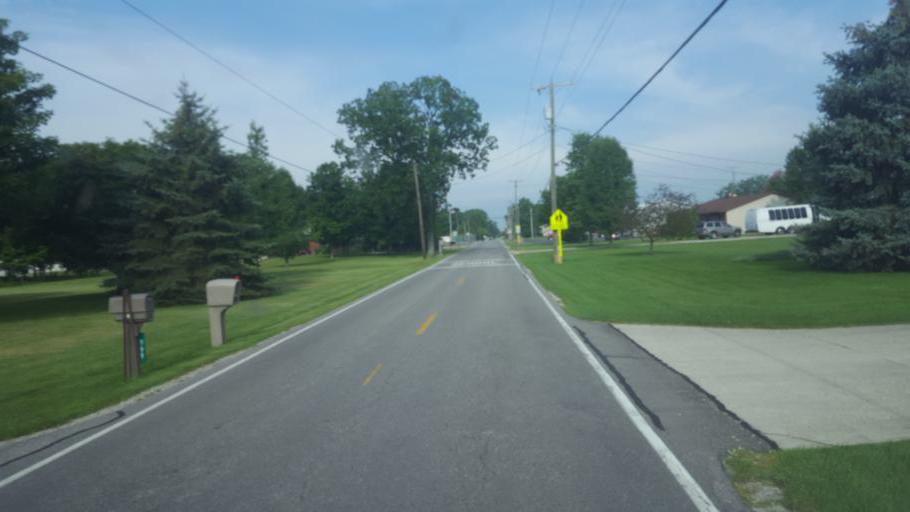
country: US
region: Ohio
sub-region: Marion County
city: Marion
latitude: 40.5202
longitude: -83.1337
